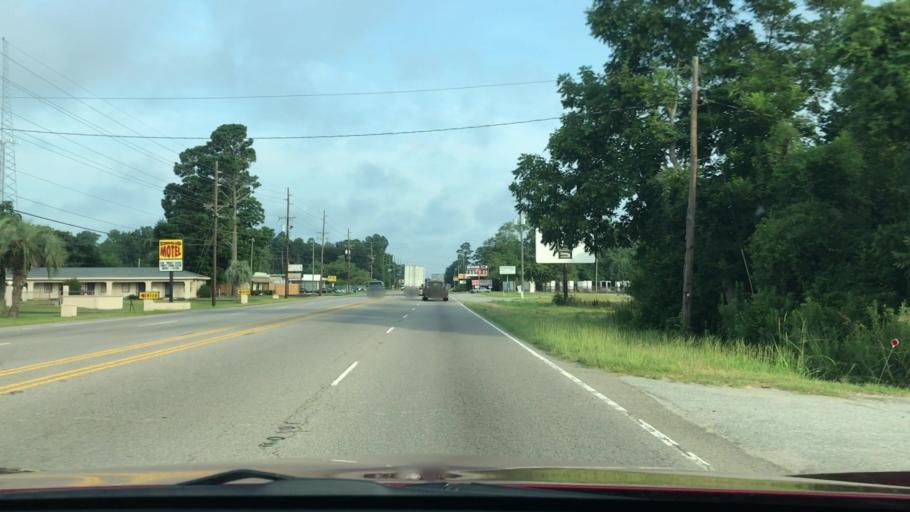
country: US
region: South Carolina
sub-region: Orangeburg County
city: Wilkinson Heights
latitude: 33.4772
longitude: -80.8164
